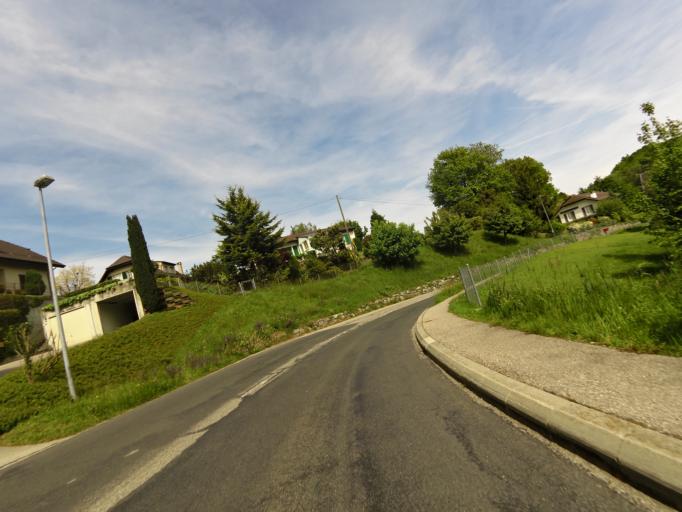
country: CH
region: Vaud
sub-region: Nyon District
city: Genolier
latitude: 46.4359
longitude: 6.2189
